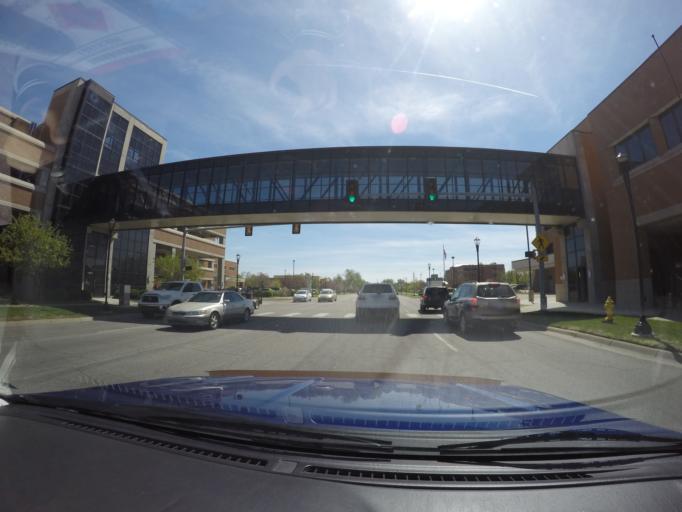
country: US
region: Kansas
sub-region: Saline County
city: Salina
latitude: 38.8331
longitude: -97.6092
